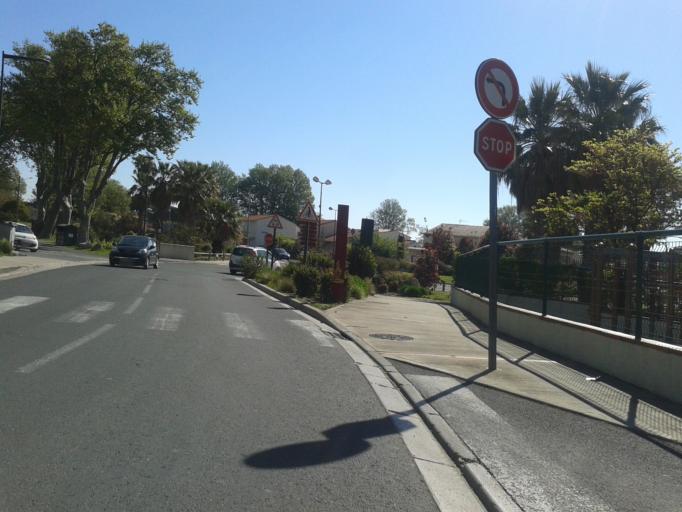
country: FR
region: Languedoc-Roussillon
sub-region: Departement des Pyrenees-Orientales
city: Toulouges
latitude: 42.6724
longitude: 2.8325
